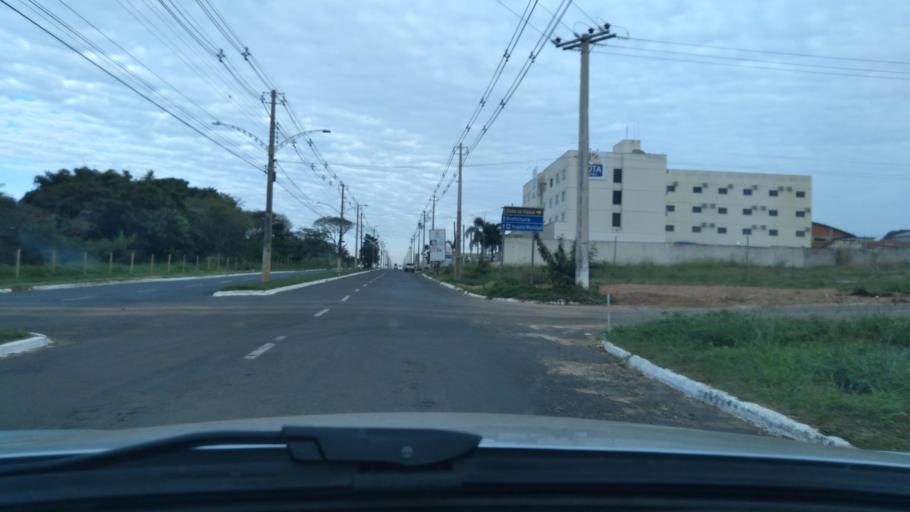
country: YE
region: Al Mahrah
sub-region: Shahan
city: Shihan as Sufla
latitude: 17.5586
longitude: 52.5347
